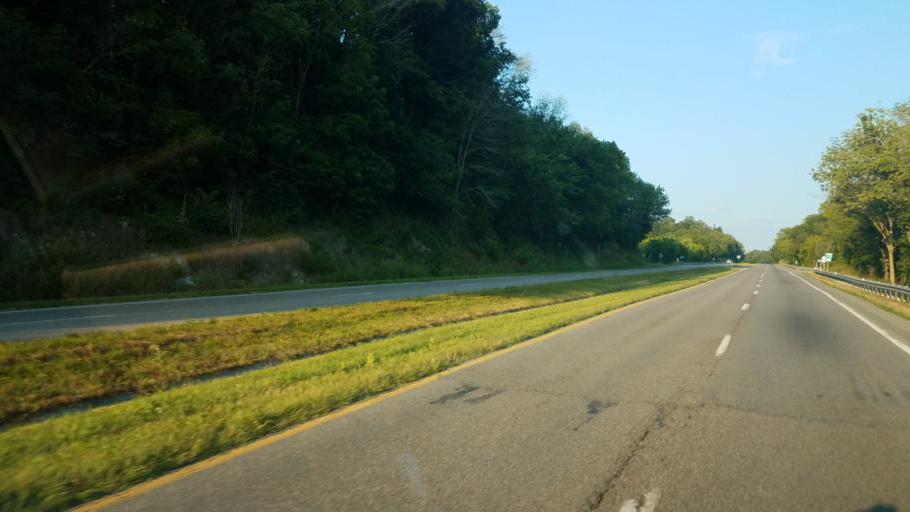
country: US
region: Tennessee
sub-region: Hawkins County
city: Mount Carmel
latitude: 36.6415
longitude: -82.7204
